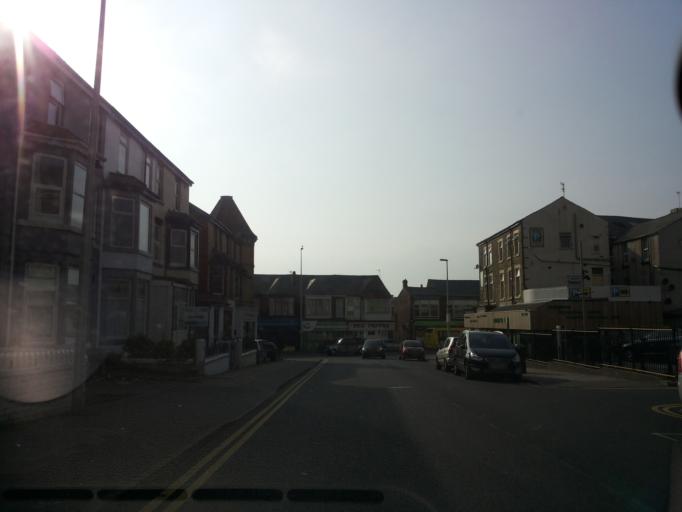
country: GB
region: England
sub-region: Blackpool
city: Blackpool
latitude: 53.8123
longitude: -3.0487
